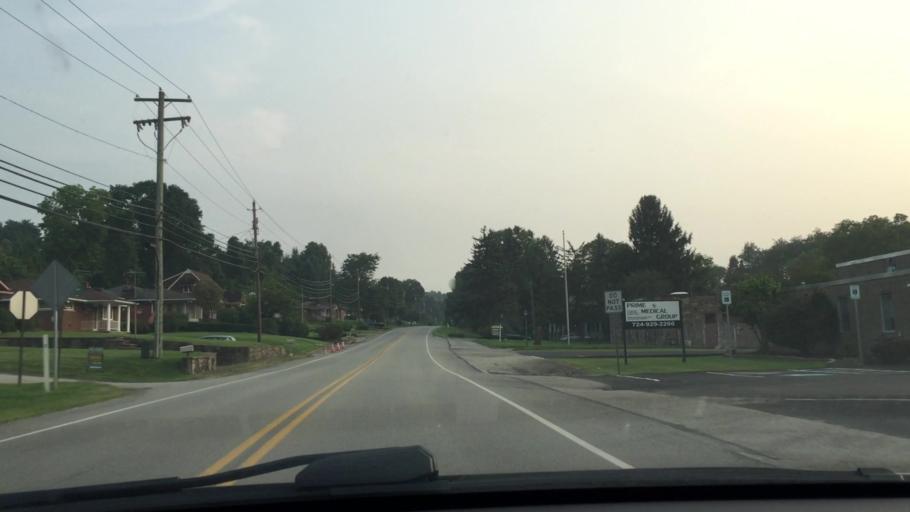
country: US
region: Pennsylvania
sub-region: Westmoreland County
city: Fellsburg
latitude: 40.1759
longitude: -79.8060
